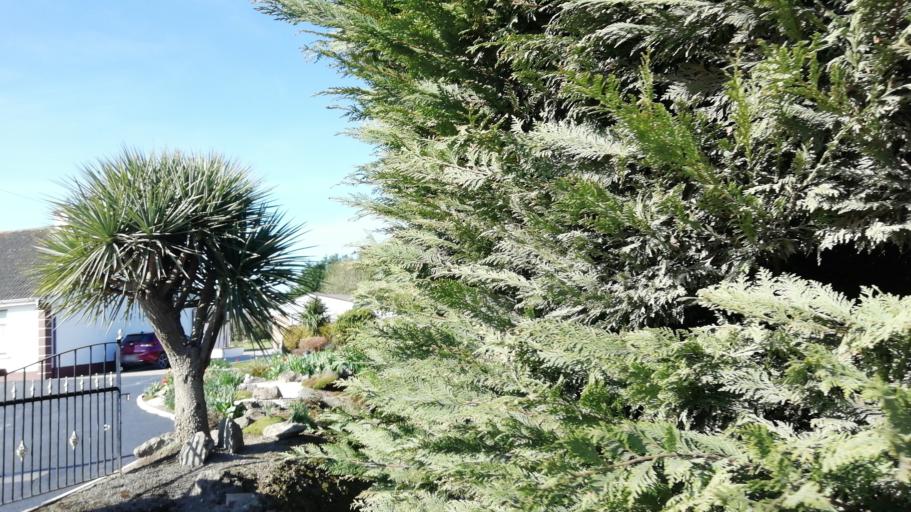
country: IE
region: Leinster
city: Malahide
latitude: 53.4347
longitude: -6.1671
